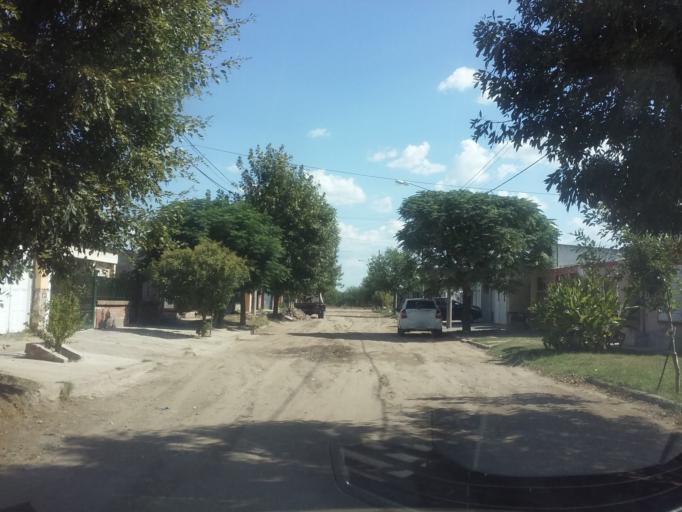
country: AR
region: La Pampa
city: Santa Rosa
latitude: -36.6500
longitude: -64.2938
